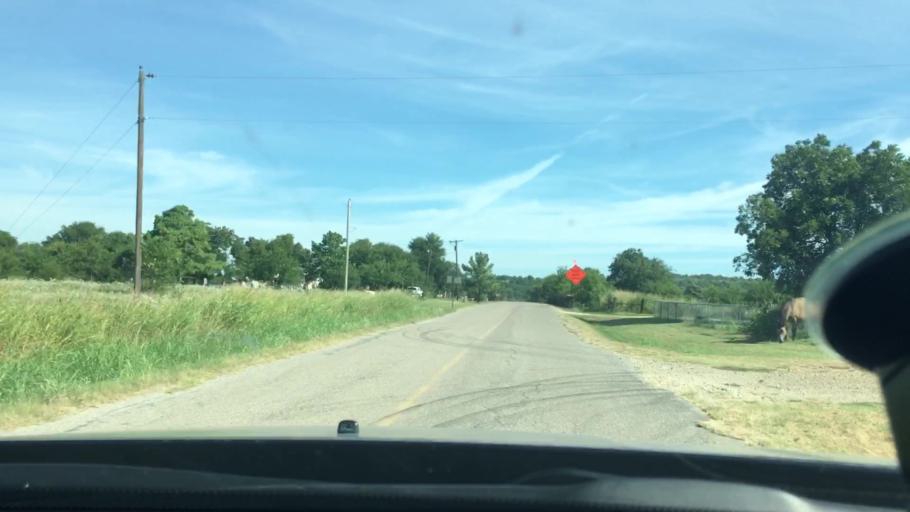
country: US
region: Oklahoma
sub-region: Carter County
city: Lone Grove
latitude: 34.3302
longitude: -97.2825
